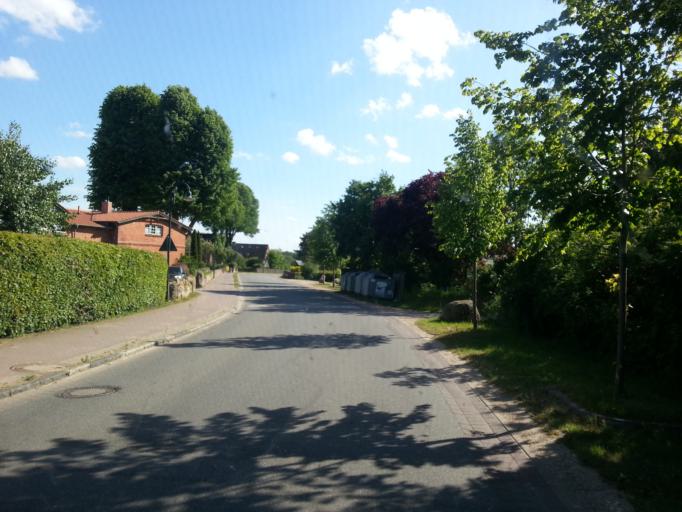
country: DE
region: Schleswig-Holstein
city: Scharbeutz
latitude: 54.0019
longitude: 10.7233
